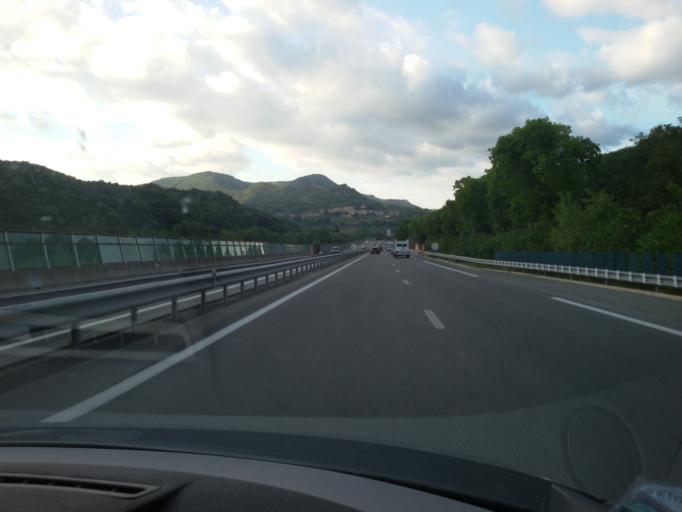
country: FR
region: Languedoc-Roussillon
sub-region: Departement de l'Herault
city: Lodeve
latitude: 43.7477
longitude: 3.3308
